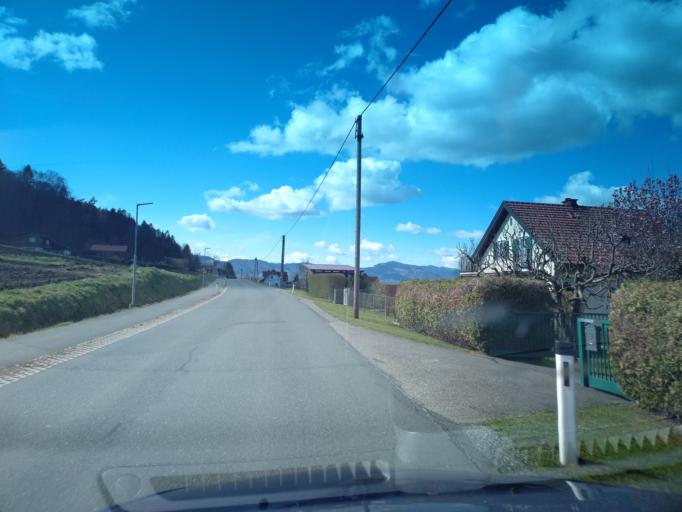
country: AT
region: Styria
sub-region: Politischer Bezirk Leibnitz
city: Sankt Johann im Saggautal
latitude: 46.7137
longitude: 15.4090
